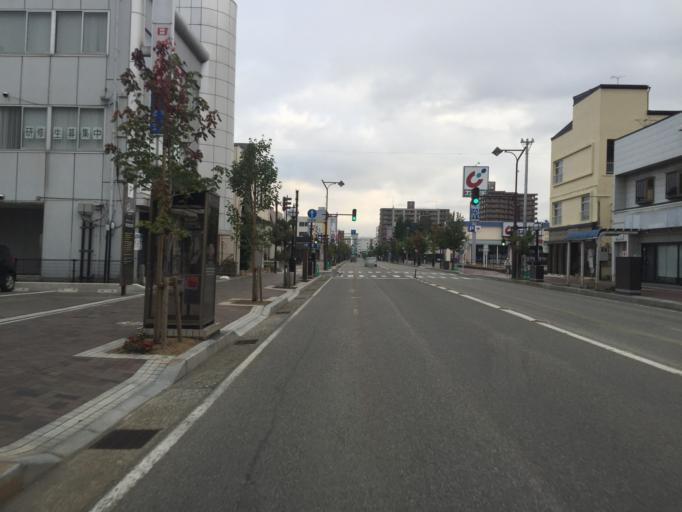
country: JP
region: Fukushima
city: Kitakata
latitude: 37.5011
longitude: 139.9298
